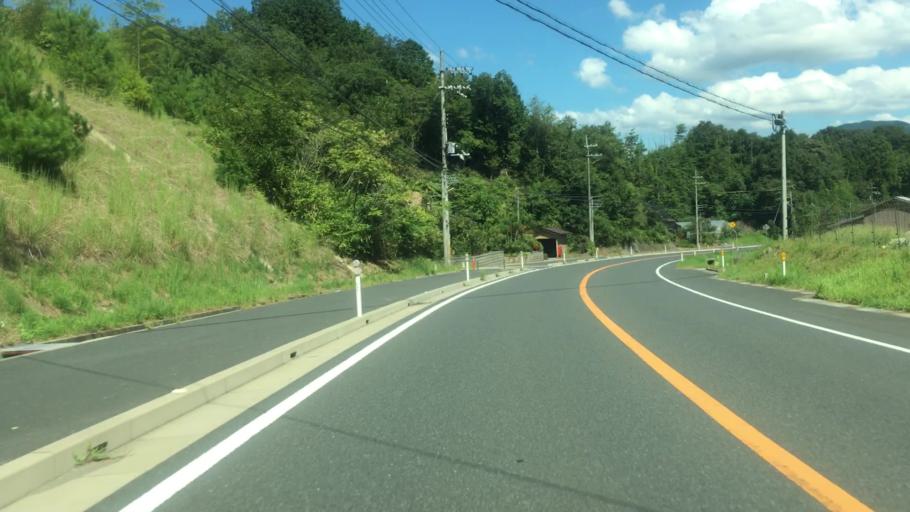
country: JP
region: Hyogo
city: Toyooka
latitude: 35.5910
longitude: 134.9371
